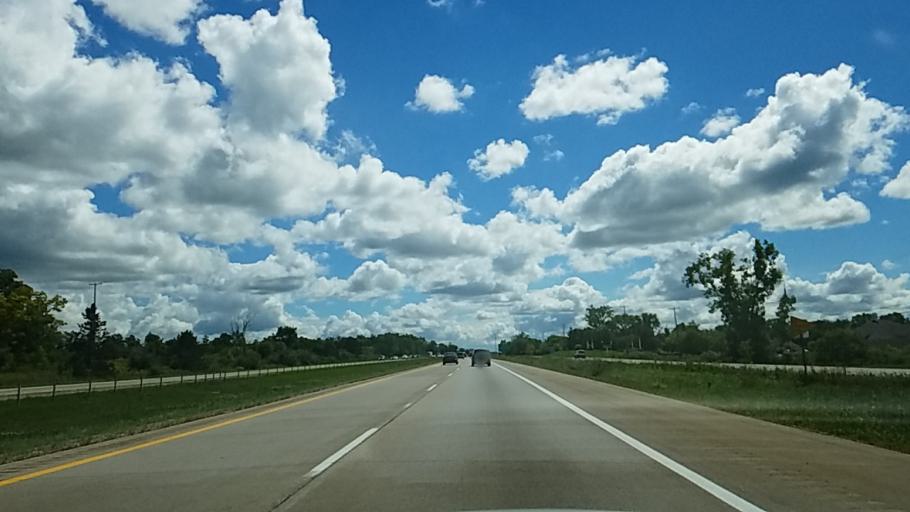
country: US
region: Michigan
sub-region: Genesee County
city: Fenton
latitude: 42.6966
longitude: -83.7616
